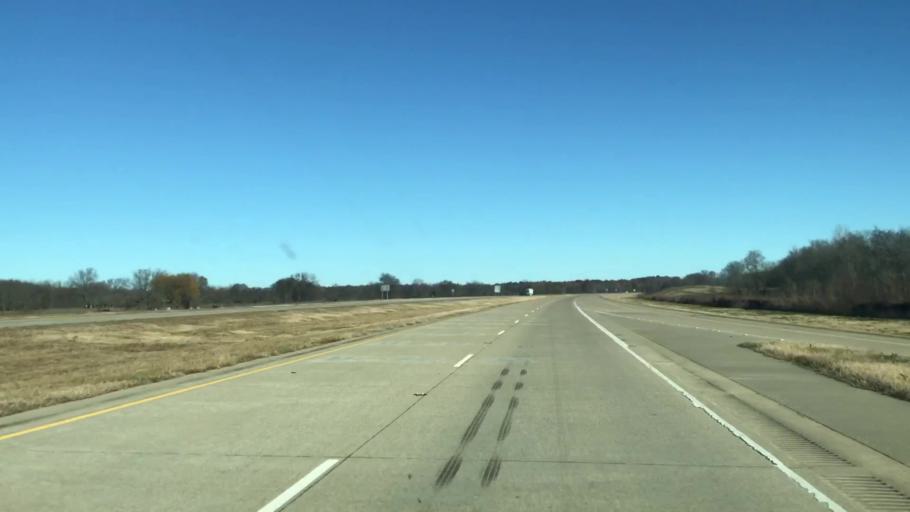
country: US
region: Louisiana
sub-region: Caddo Parish
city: Oil City
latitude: 32.7719
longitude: -93.8891
